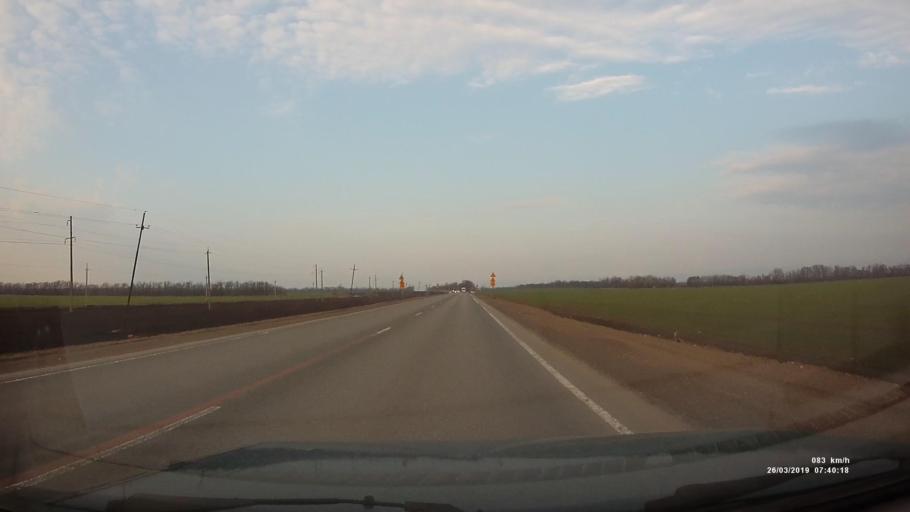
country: RU
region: Rostov
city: Novobessergenovka
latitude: 47.1951
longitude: 38.6499
